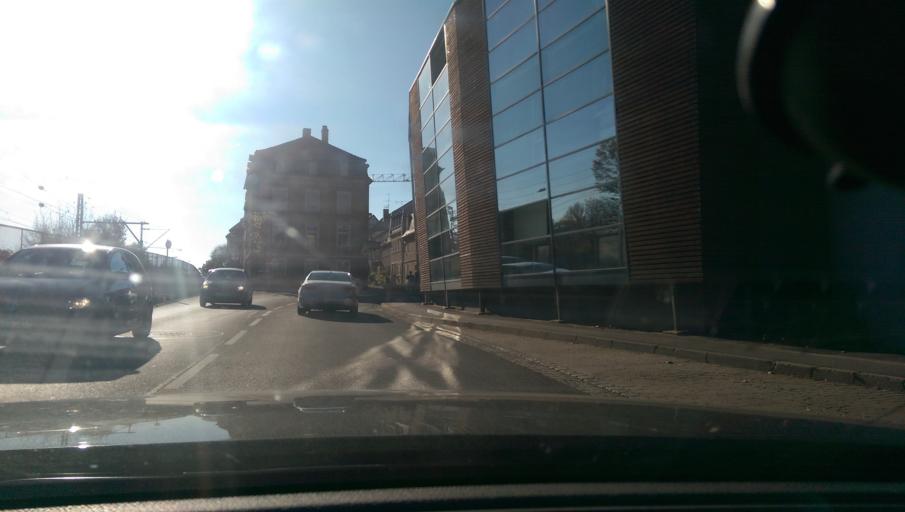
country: DE
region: Bavaria
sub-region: Regierungsbezirk Unterfranken
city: Schweinfurt
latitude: 50.0429
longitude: 10.2343
